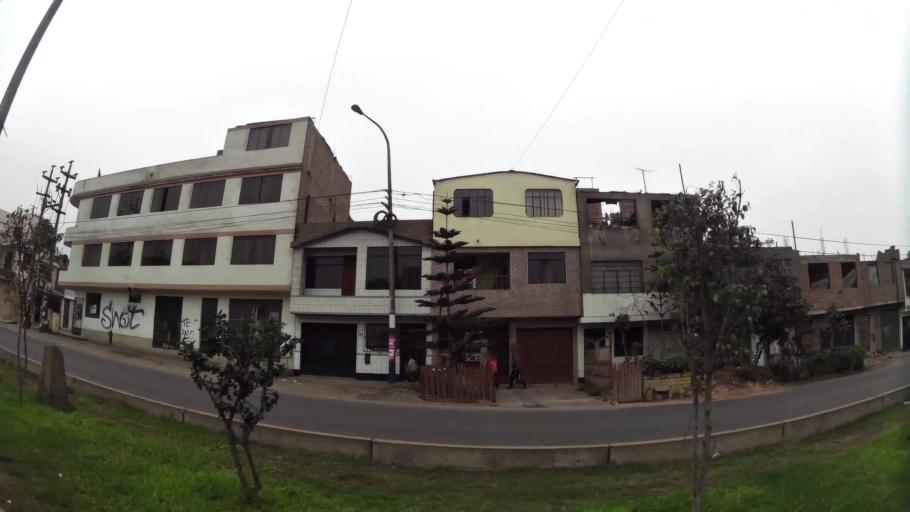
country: PE
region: Lima
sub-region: Lima
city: Independencia
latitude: -11.9584
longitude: -76.9839
